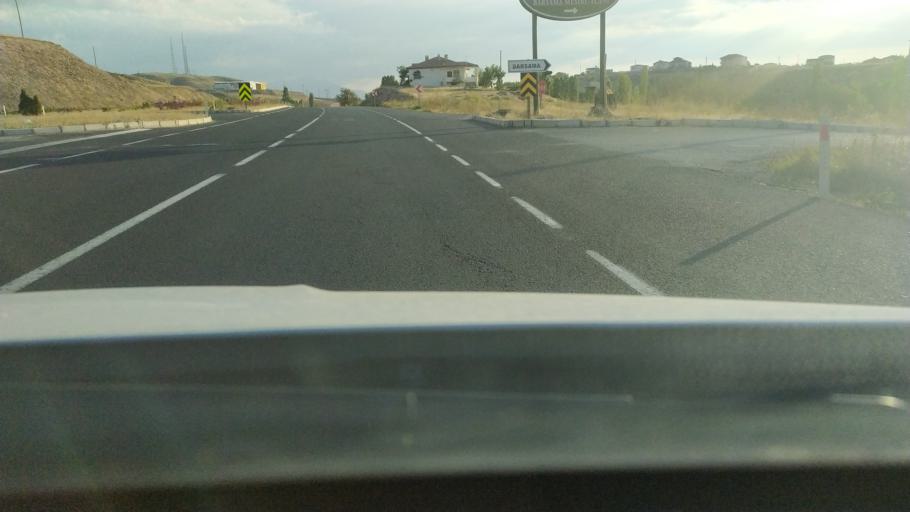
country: TR
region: Kayseri
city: Muncusun
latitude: 38.8710
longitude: 35.6993
